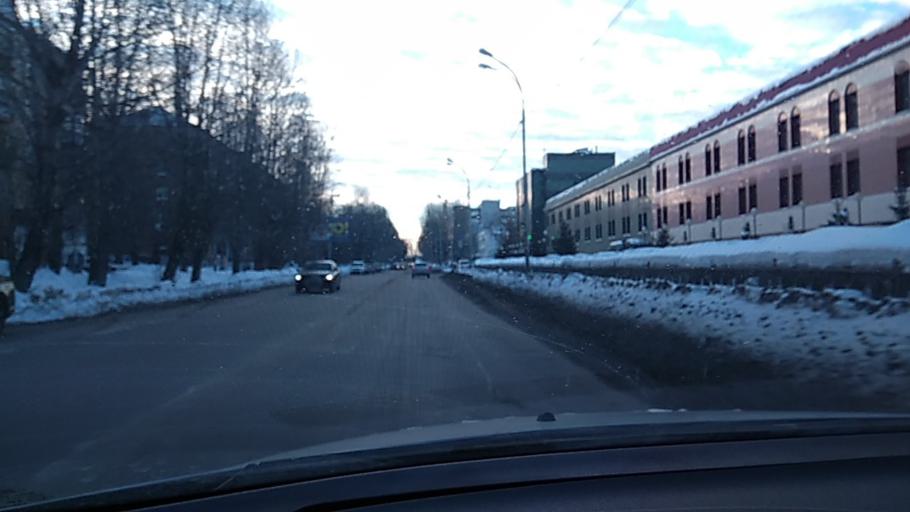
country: RU
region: Sverdlovsk
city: Yekaterinburg
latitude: 56.8386
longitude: 60.6470
